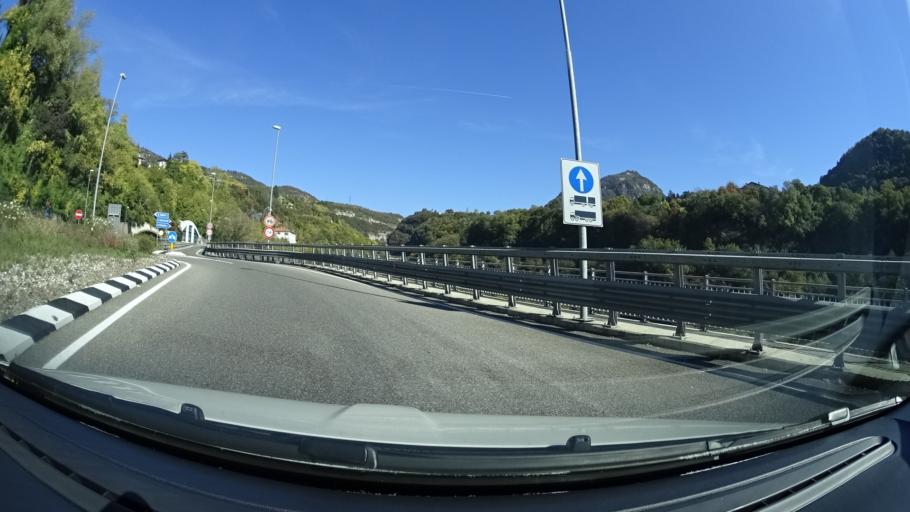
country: IT
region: Trentino-Alto Adige
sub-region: Provincia di Trento
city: Povo
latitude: 46.0754
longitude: 11.1508
